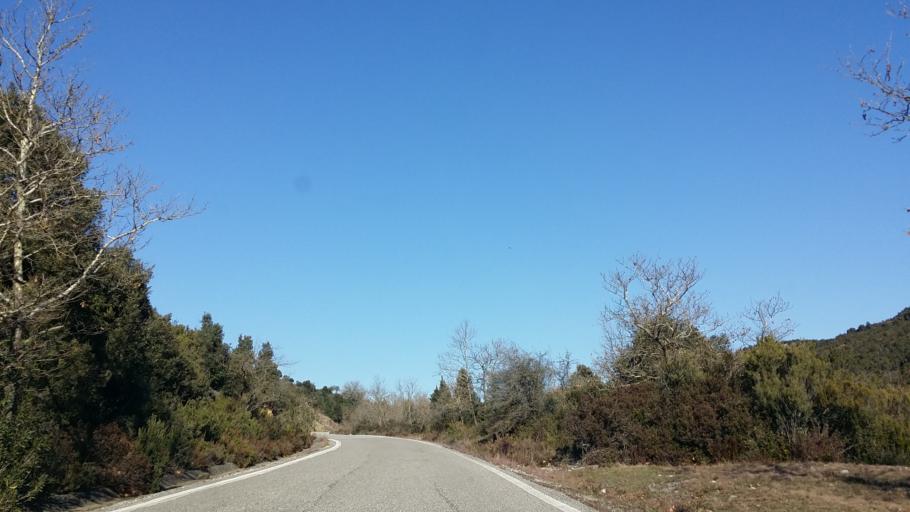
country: GR
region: West Greece
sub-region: Nomos Aitolias kai Akarnanias
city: Lepenou
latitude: 38.7822
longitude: 21.3344
